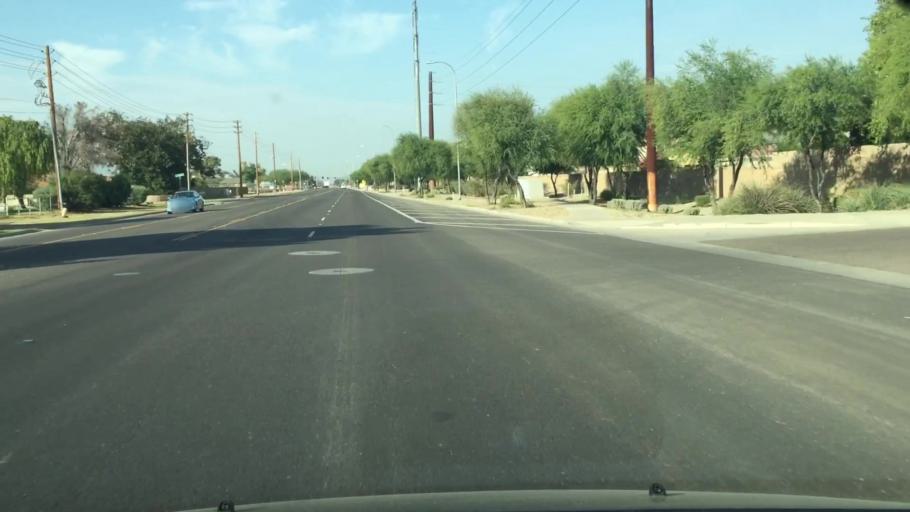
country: US
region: Arizona
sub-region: Maricopa County
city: Laveen
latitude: 33.3630
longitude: -112.1631
